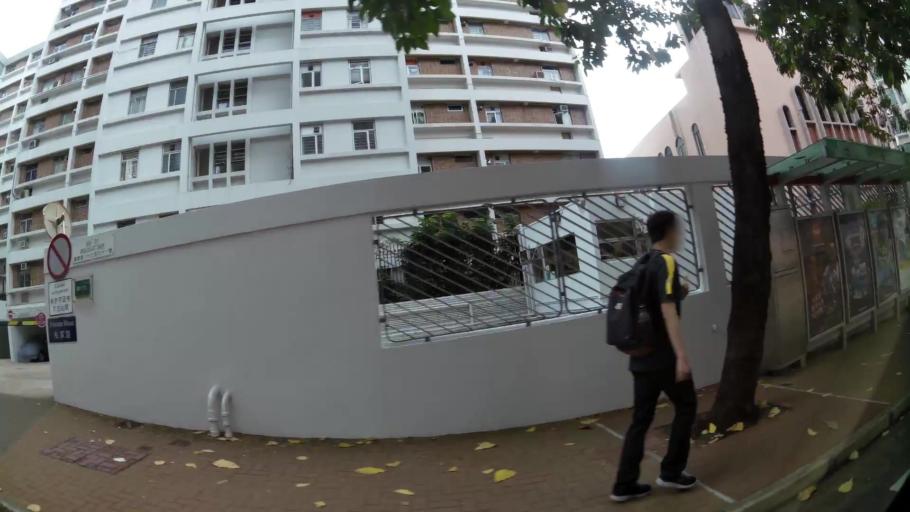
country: HK
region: Wong Tai Sin
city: Wong Tai Sin
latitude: 22.3406
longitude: 114.1826
